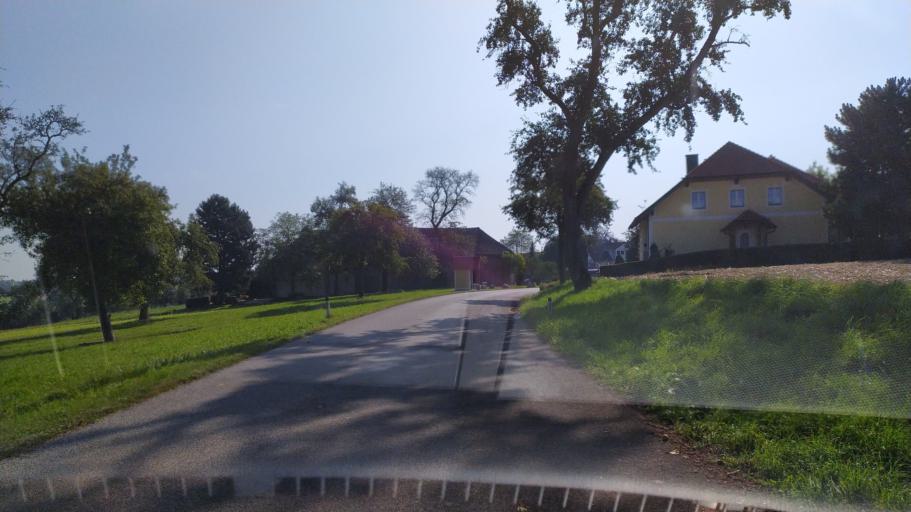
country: AT
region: Lower Austria
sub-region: Politischer Bezirk Amstetten
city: Zeillern
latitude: 48.1121
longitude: 14.7349
